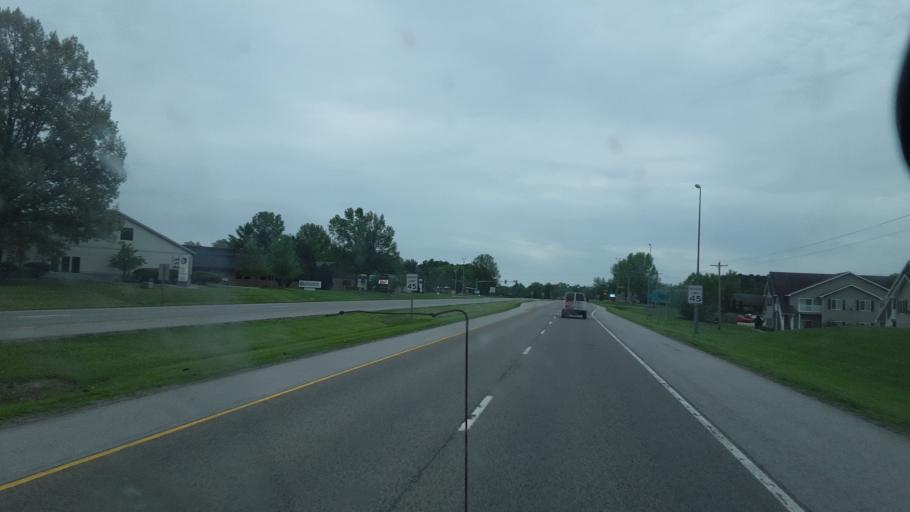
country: US
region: Illinois
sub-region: Jackson County
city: Carbondale
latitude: 37.7401
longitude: -89.2551
